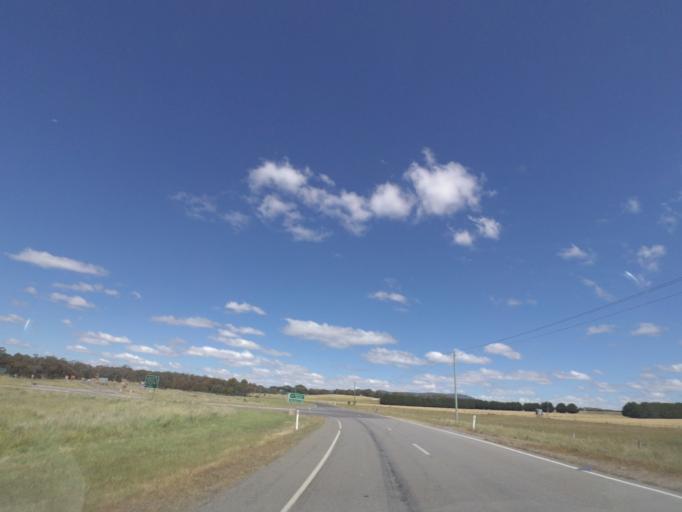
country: AU
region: Victoria
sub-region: Hume
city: Sunbury
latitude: -37.2960
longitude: 144.4994
